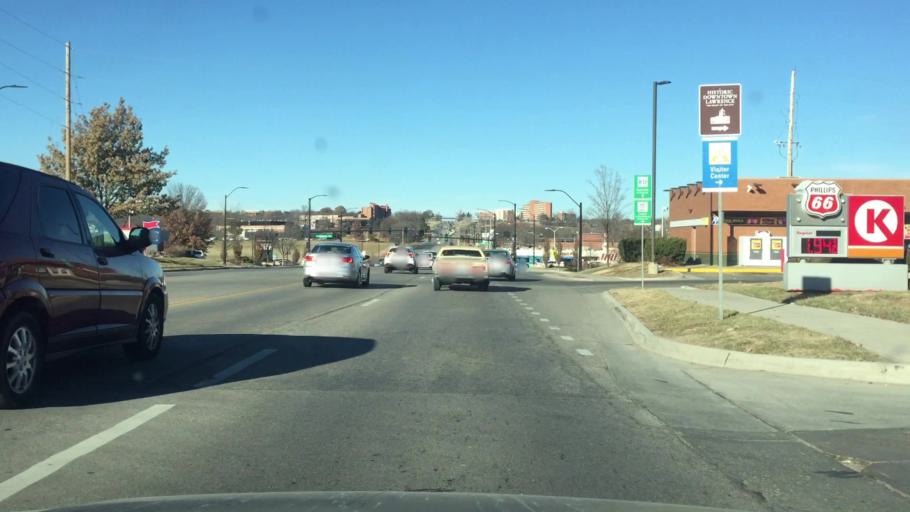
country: US
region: Kansas
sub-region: Douglas County
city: Lawrence
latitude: 38.9411
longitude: -95.2604
